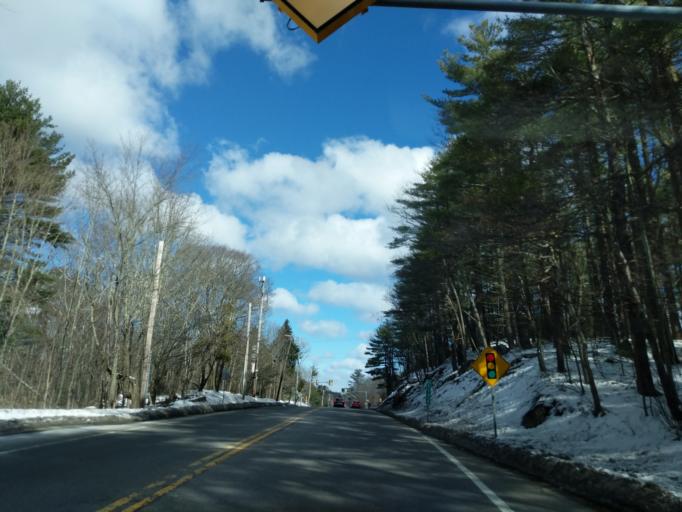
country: US
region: Massachusetts
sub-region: Norfolk County
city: Milton
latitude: 42.2227
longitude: -71.0705
